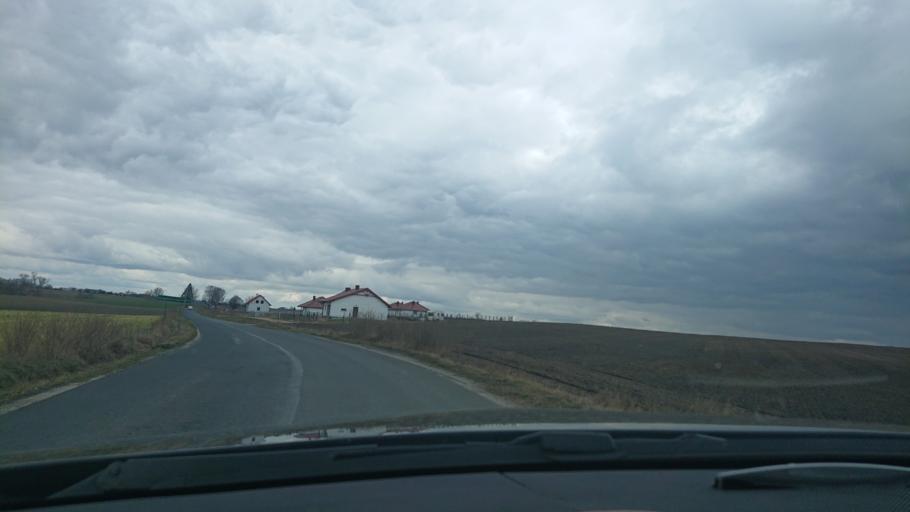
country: PL
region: Greater Poland Voivodeship
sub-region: Powiat gnieznienski
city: Gniezno
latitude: 52.5771
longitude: 17.6689
